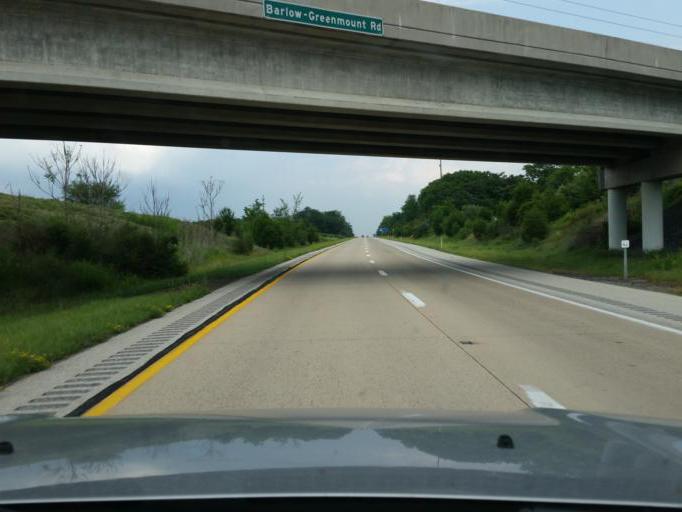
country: US
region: Pennsylvania
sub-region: Adams County
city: Gettysburg
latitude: 39.7649
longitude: -77.2585
